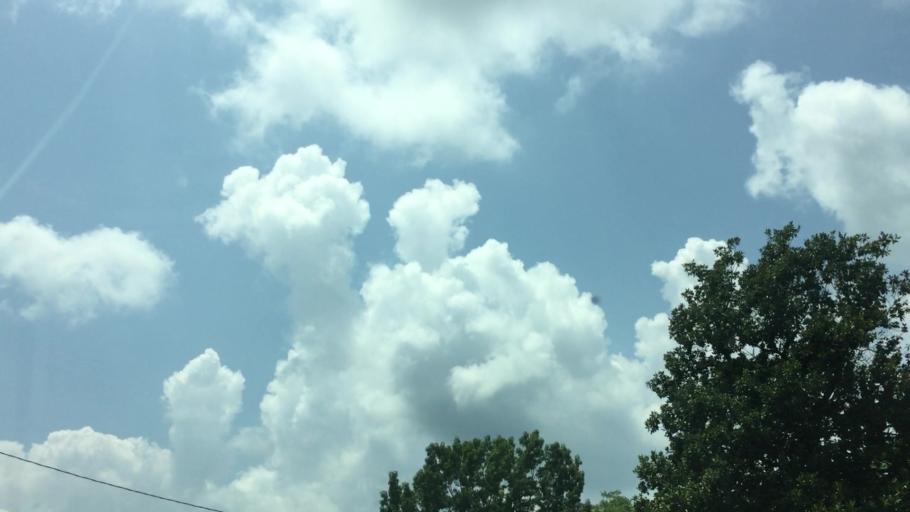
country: US
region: Georgia
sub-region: Carroll County
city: Villa Rica
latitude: 33.6238
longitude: -84.8624
